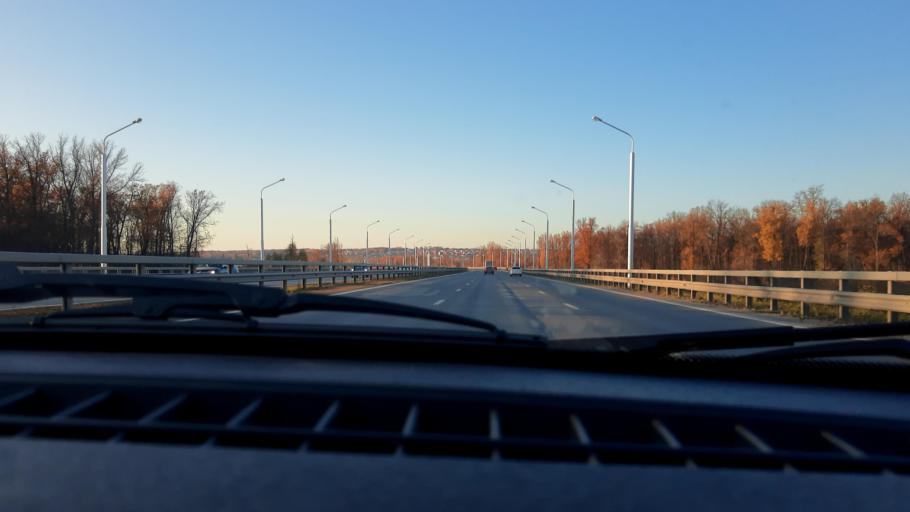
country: RU
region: Bashkortostan
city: Mikhaylovka
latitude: 54.7902
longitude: 55.9073
